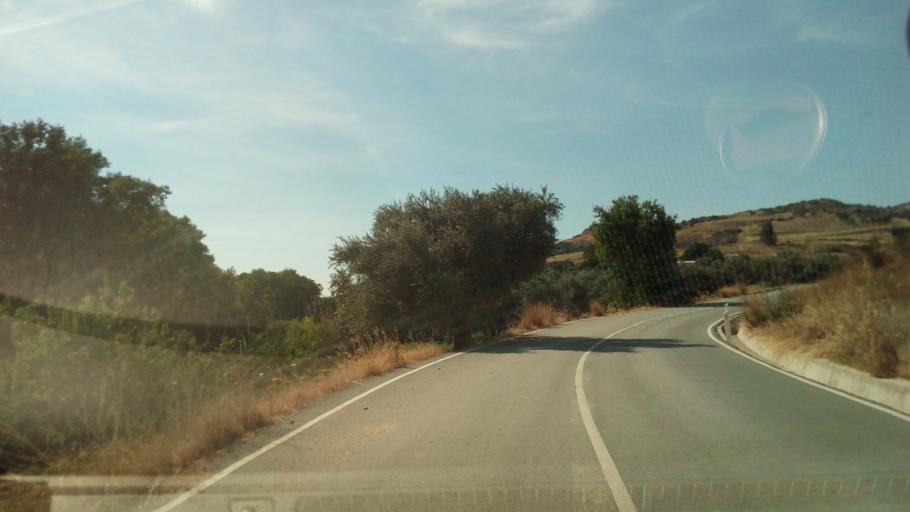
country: CY
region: Pafos
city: Polis
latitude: 34.9560
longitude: 32.5119
